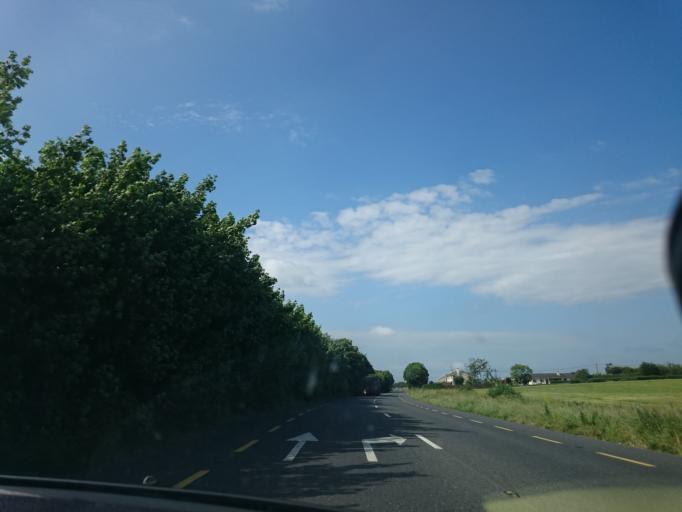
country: IE
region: Leinster
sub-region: Kilkenny
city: Kilkenny
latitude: 52.5939
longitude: -7.2418
